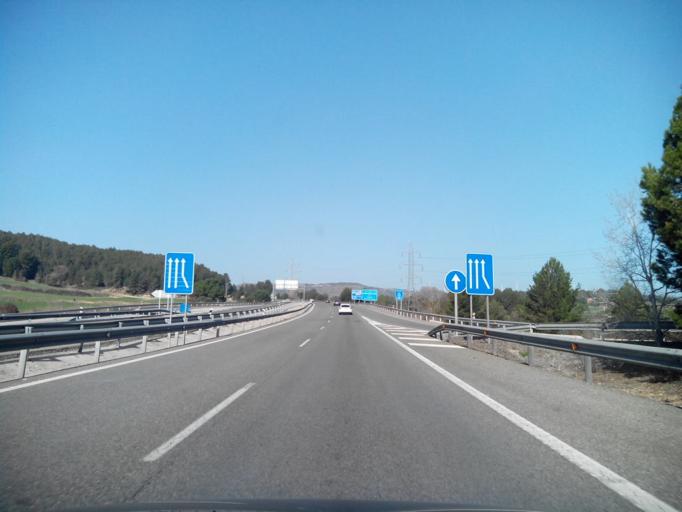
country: ES
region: Catalonia
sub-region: Provincia de Barcelona
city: Odena
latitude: 41.6010
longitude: 1.6347
